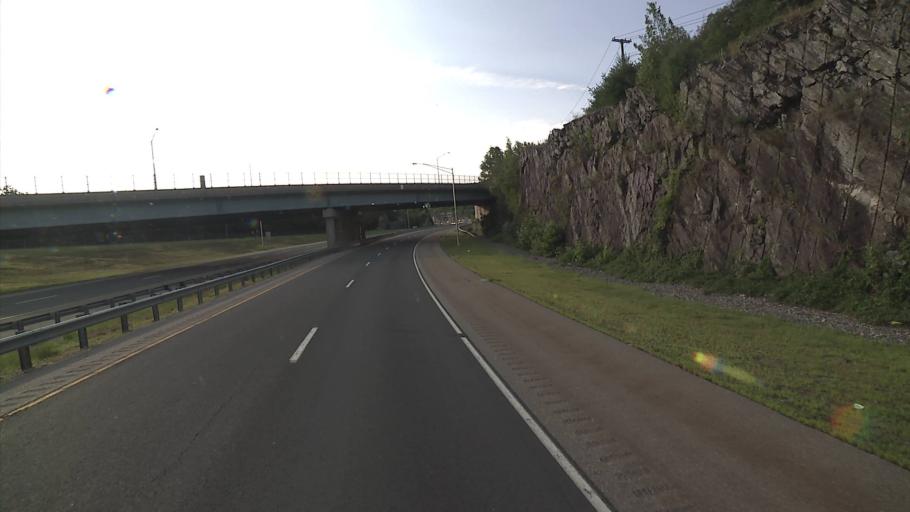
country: US
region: Connecticut
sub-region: New London County
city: Norwich
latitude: 41.5619
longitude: -72.1277
